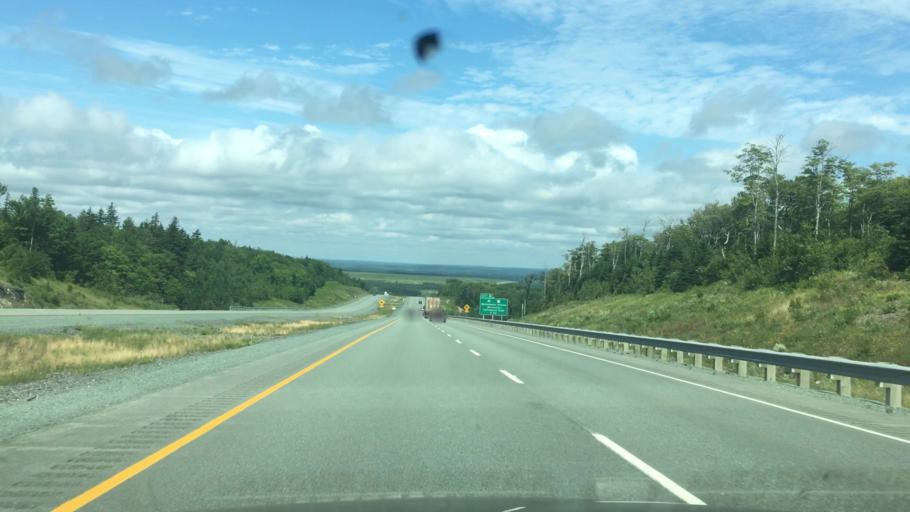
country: CA
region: Nova Scotia
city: Oxford
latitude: 45.5879
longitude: -63.7210
